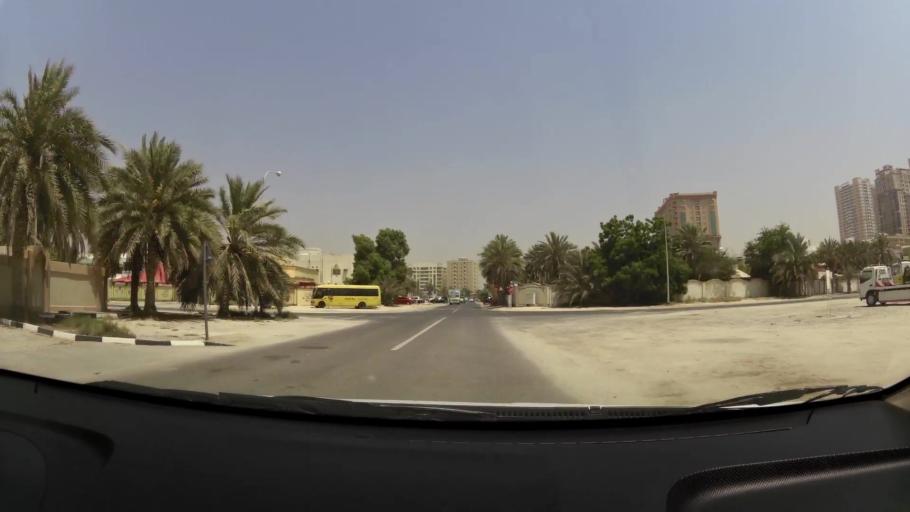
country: AE
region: Ajman
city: Ajman
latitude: 25.4006
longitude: 55.4316
